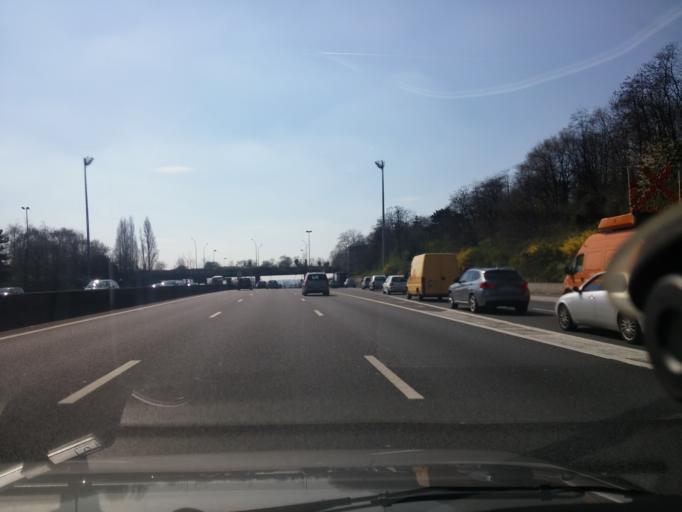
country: FR
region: Ile-de-France
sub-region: Departement du Val-de-Marne
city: Joinville-le-Pont
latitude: 48.8191
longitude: 2.4578
